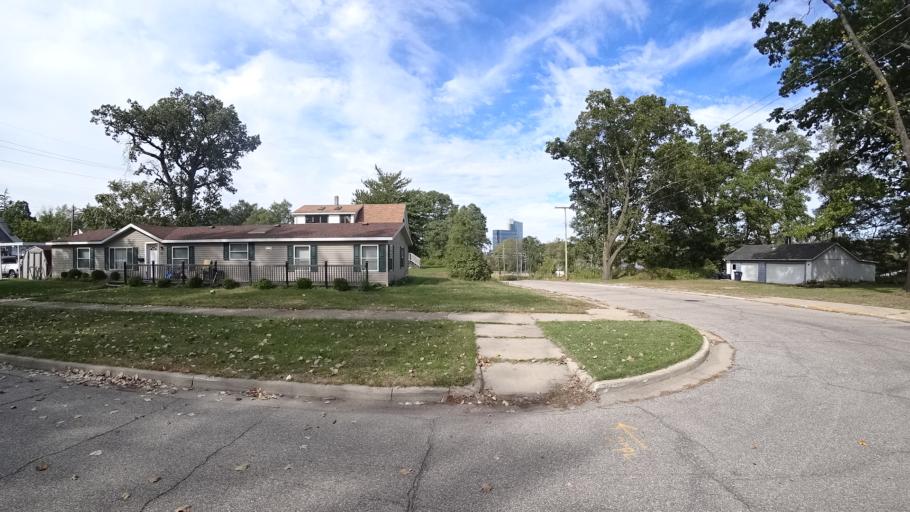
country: US
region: Indiana
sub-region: LaPorte County
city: Michigan City
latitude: 41.7157
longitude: -86.8851
